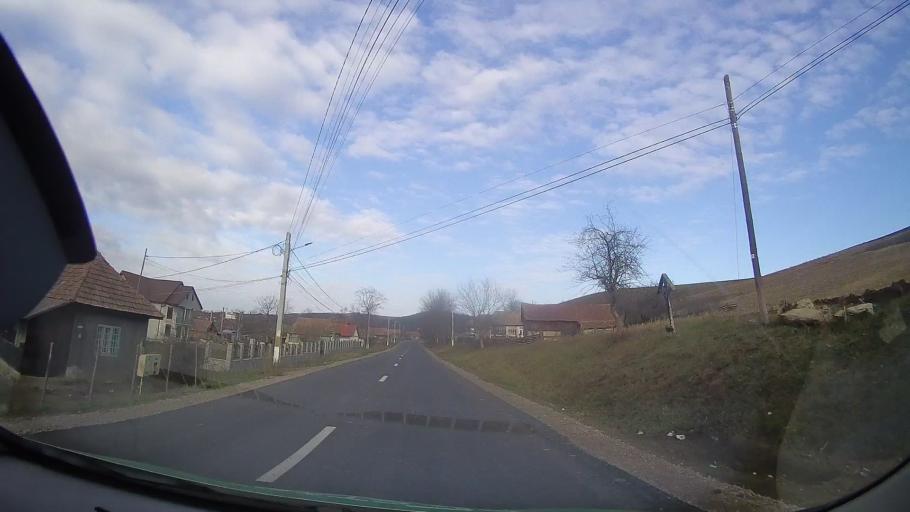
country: RO
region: Mures
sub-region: Comuna Iclanzel
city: Iclanzel
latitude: 46.5185
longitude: 24.2739
